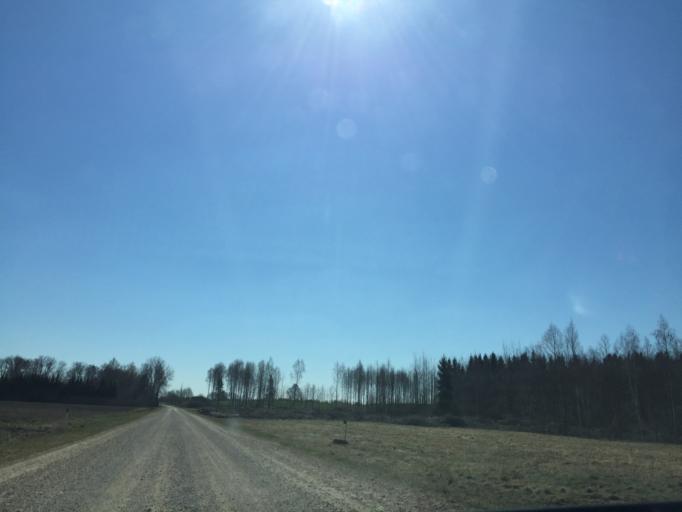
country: EE
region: Viljandimaa
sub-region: Viiratsi vald
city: Viiratsi
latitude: 58.3642
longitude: 25.7516
